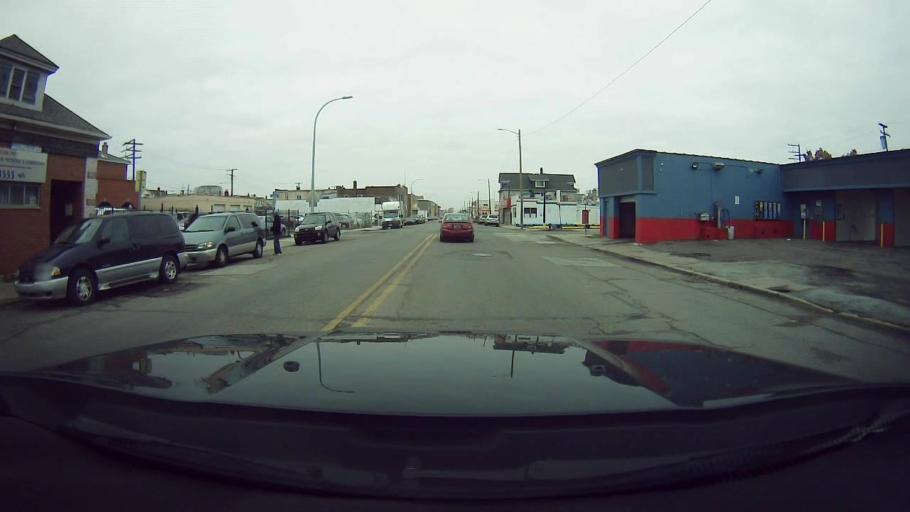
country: US
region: Michigan
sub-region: Wayne County
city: Hamtramck
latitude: 42.4044
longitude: -83.0540
